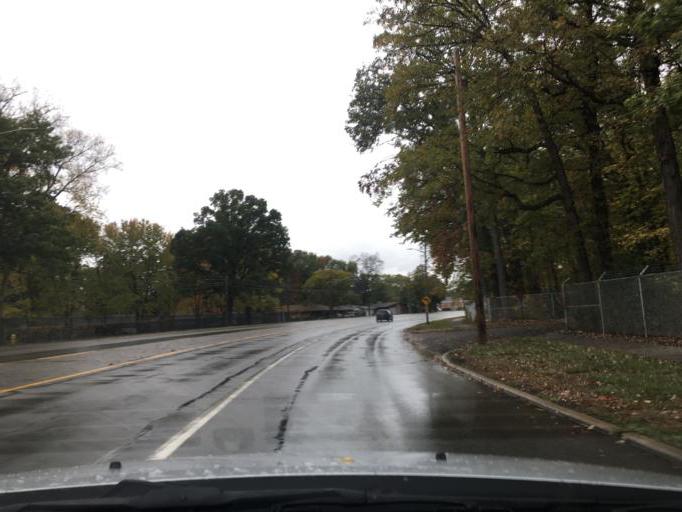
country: US
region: Michigan
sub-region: Wayne County
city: Allen Park
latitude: 42.2906
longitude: -83.2388
